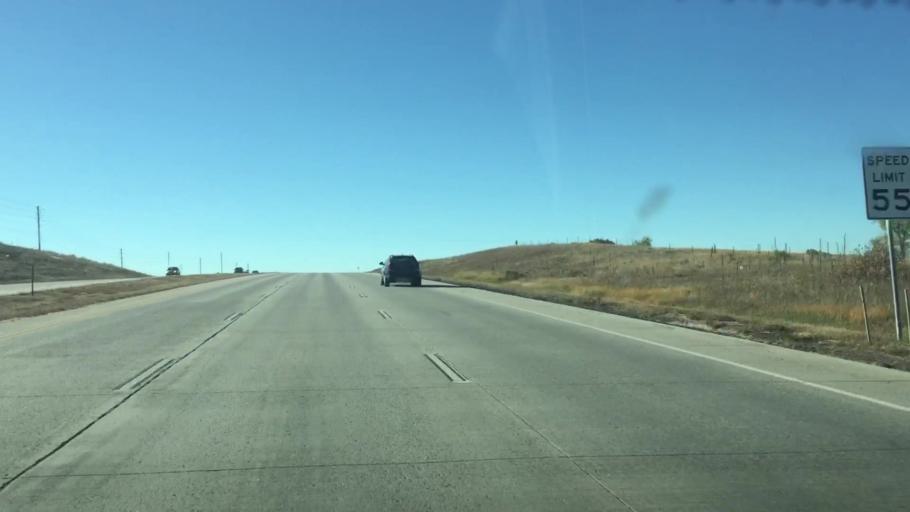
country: US
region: Colorado
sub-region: Douglas County
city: The Pinery
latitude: 39.4729
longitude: -104.7585
